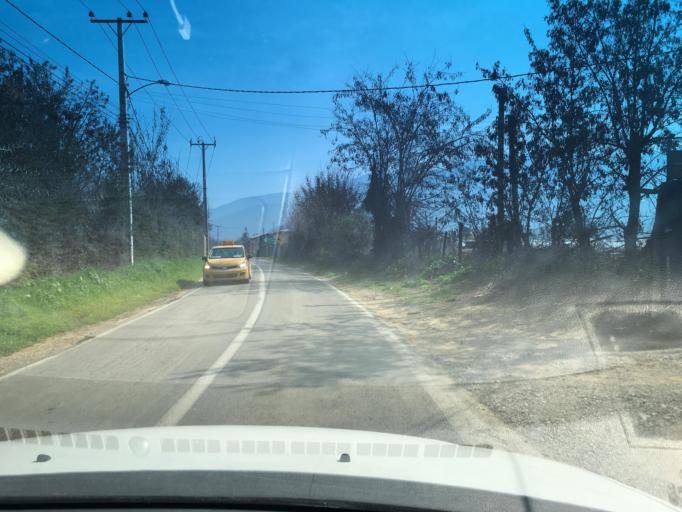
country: CL
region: Valparaiso
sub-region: Provincia de Marga Marga
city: Limache
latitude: -33.0020
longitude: -71.2324
